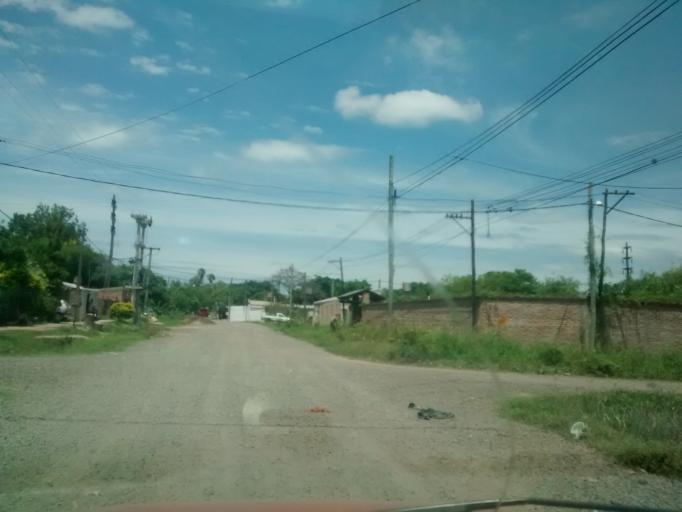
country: AR
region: Chaco
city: Resistencia
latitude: -27.4343
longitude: -58.9755
